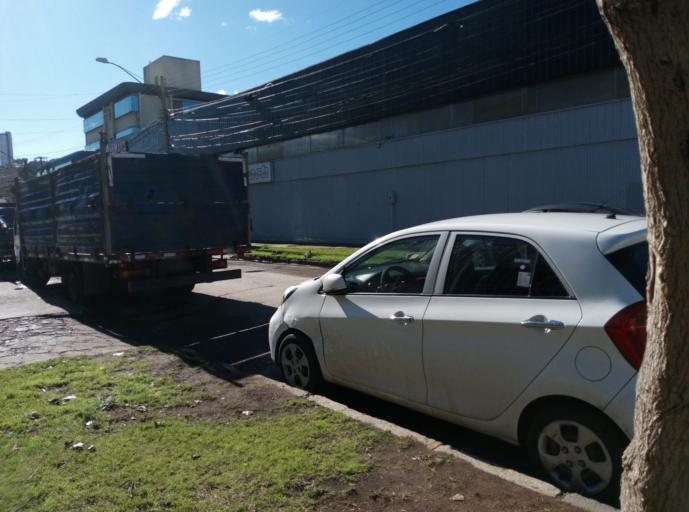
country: CL
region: Valparaiso
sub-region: Provincia de Valparaiso
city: Vina del Mar
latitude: -33.0106
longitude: -71.5439
